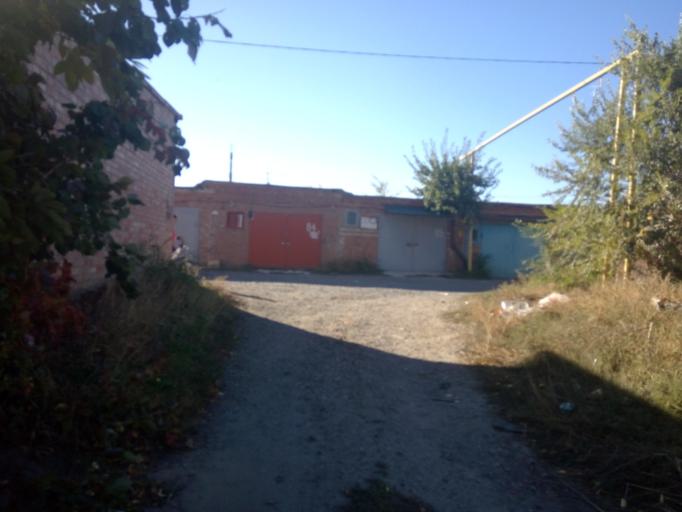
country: RU
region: Rostov
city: Bataysk
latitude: 47.1244
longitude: 39.7325
